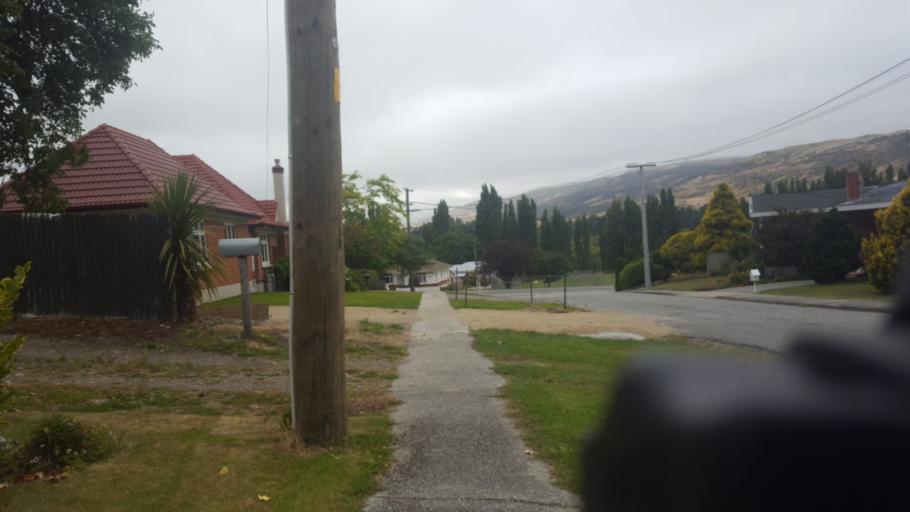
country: NZ
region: Otago
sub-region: Queenstown-Lakes District
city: Kingston
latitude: -45.5381
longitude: 169.3094
